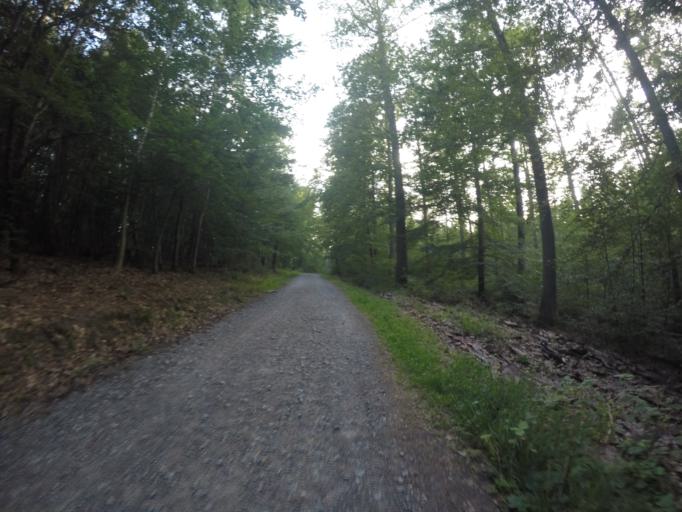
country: DE
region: Baden-Wuerttemberg
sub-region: Regierungsbezirk Stuttgart
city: Stuttgart
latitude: 48.7527
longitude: 9.1313
